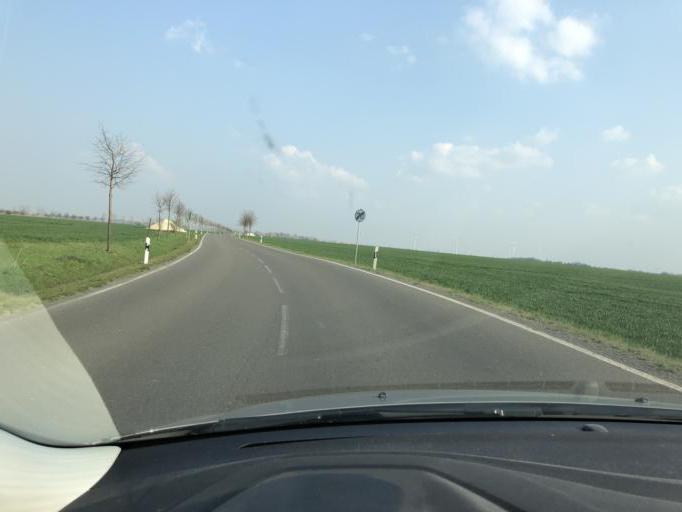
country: DE
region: Saxony
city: Rackwitz
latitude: 51.4299
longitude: 12.3873
